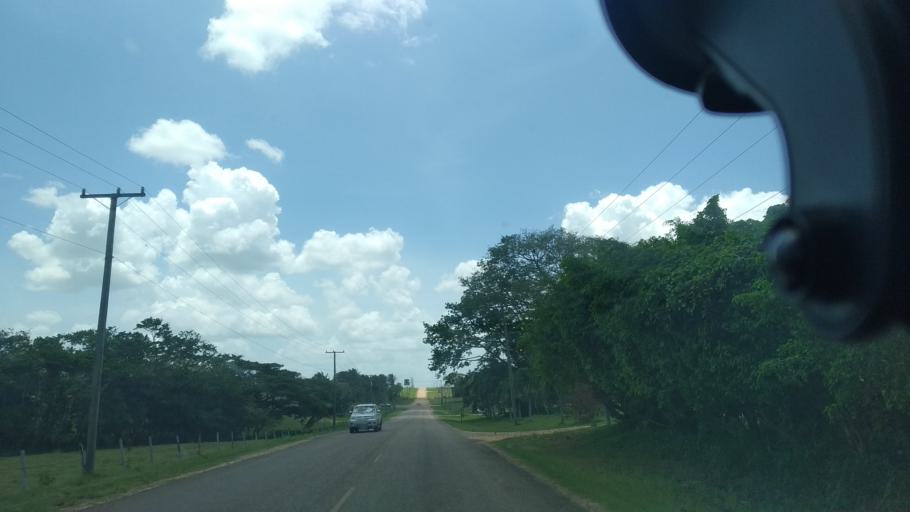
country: BZ
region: Cayo
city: San Ignacio
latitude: 17.2535
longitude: -88.9873
